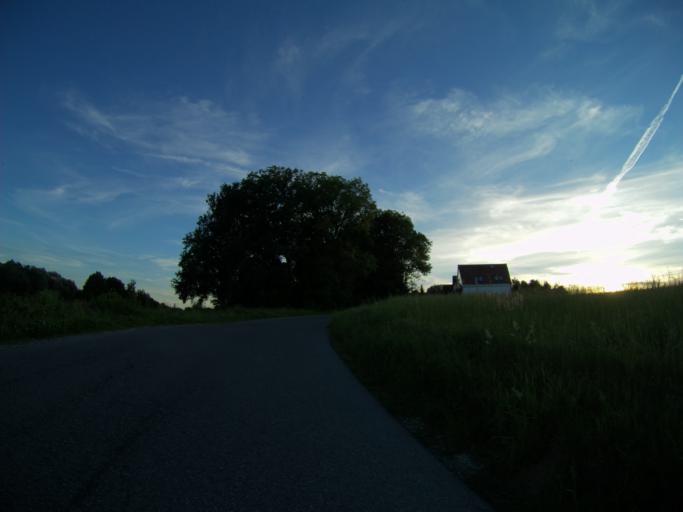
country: DE
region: Bavaria
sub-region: Upper Bavaria
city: Marzling
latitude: 48.4123
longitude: 11.7848
